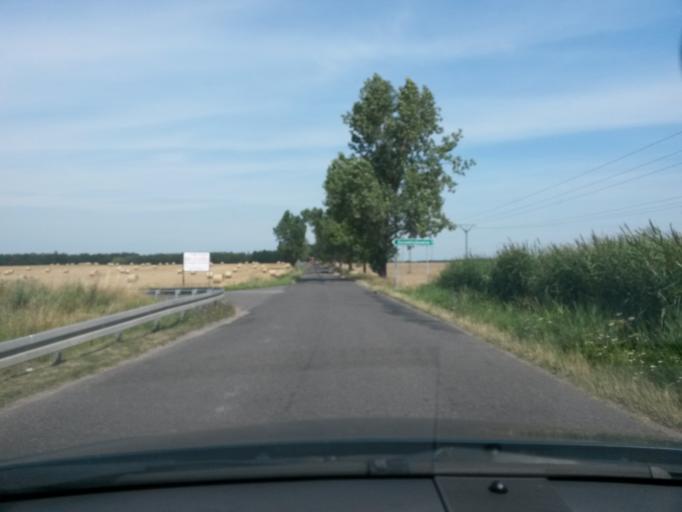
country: PL
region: Lower Silesian Voivodeship
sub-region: Powiat legnicki
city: Prochowice
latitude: 51.2270
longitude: 16.3593
